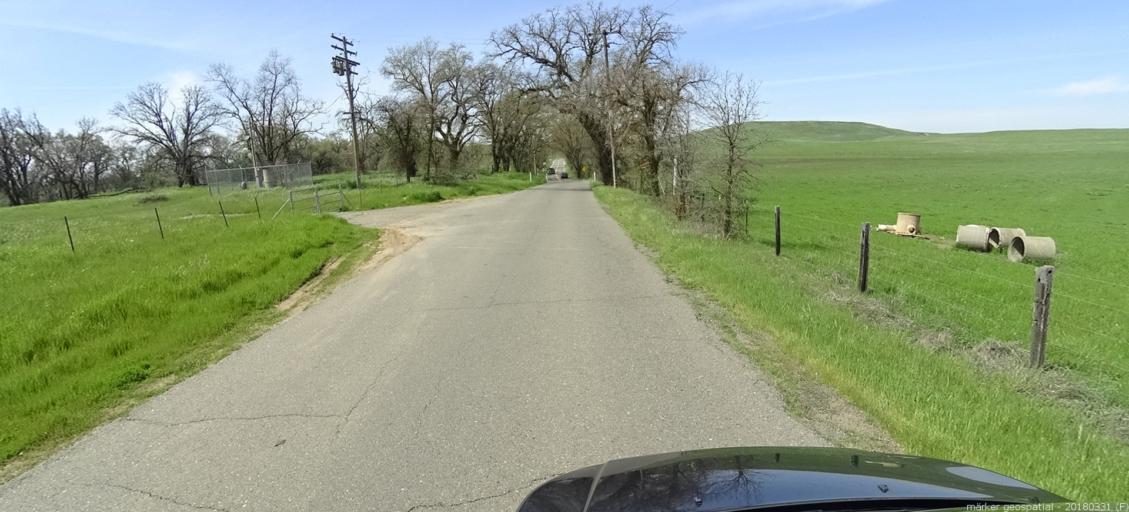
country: US
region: California
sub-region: Sacramento County
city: Rancho Murieta
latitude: 38.5030
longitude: -121.1697
